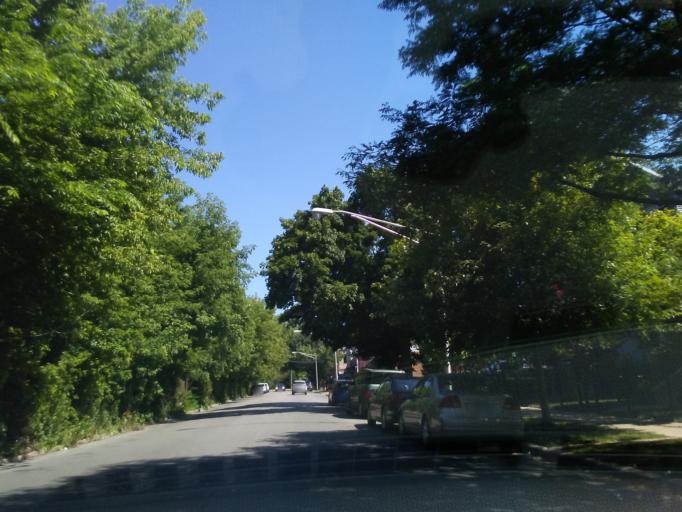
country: US
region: Illinois
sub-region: Cook County
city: Evanston
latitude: 41.9854
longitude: -87.6746
